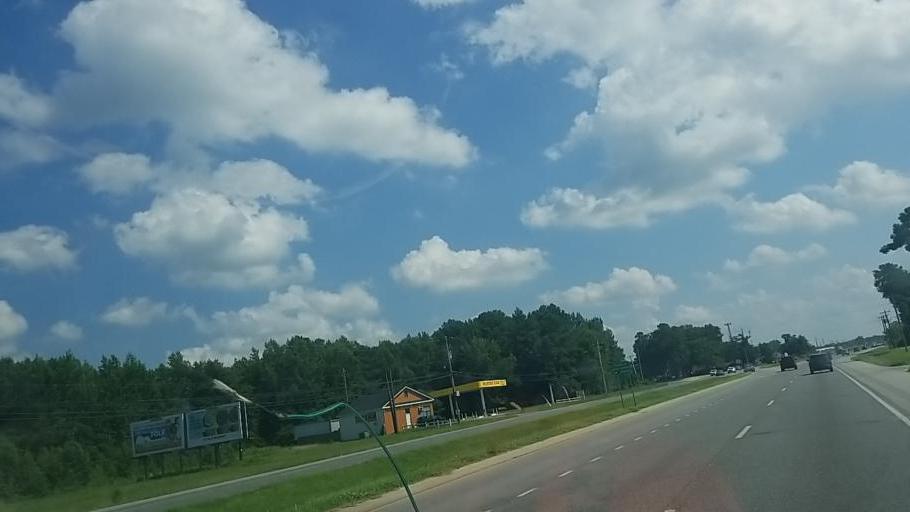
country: US
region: Delaware
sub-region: Sussex County
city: Georgetown
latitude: 38.7078
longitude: -75.4039
